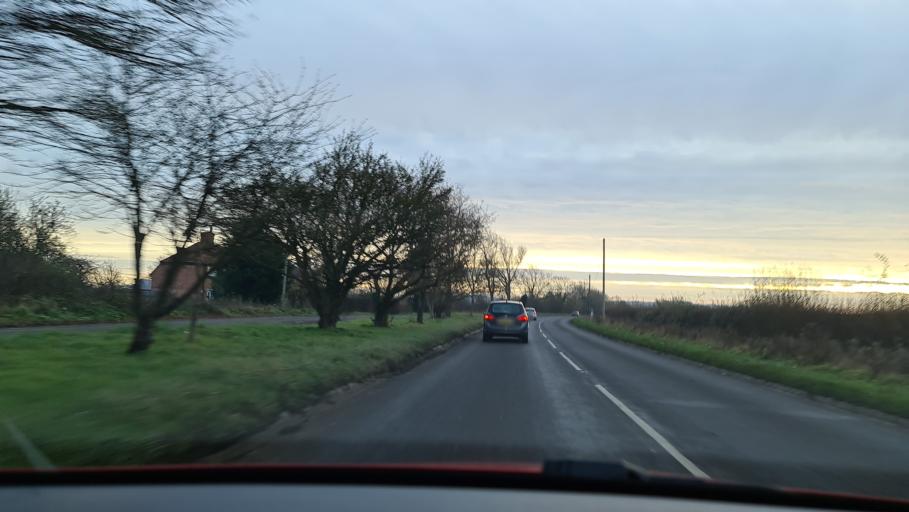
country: GB
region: England
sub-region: Buckinghamshire
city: Haddenham
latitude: 51.7508
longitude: -0.8810
